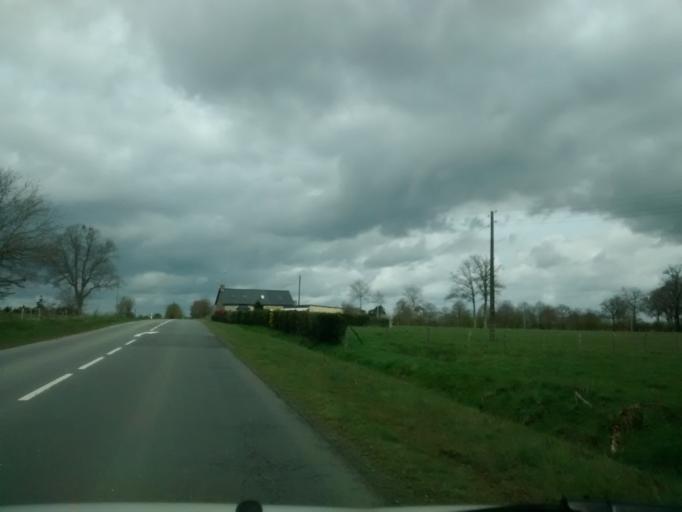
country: FR
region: Brittany
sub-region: Departement d'Ille-et-Vilaine
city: Livre-sur-Changeon
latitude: 48.2364
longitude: -1.3587
